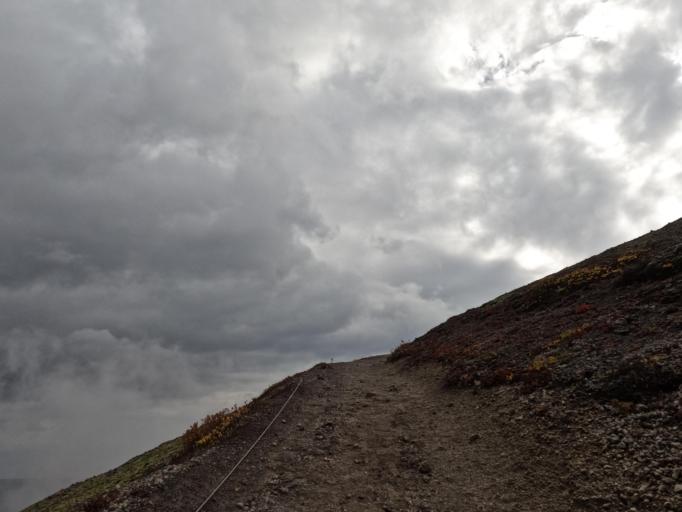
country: JP
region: Hokkaido
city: Shiraoi
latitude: 42.6925
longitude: 141.3906
